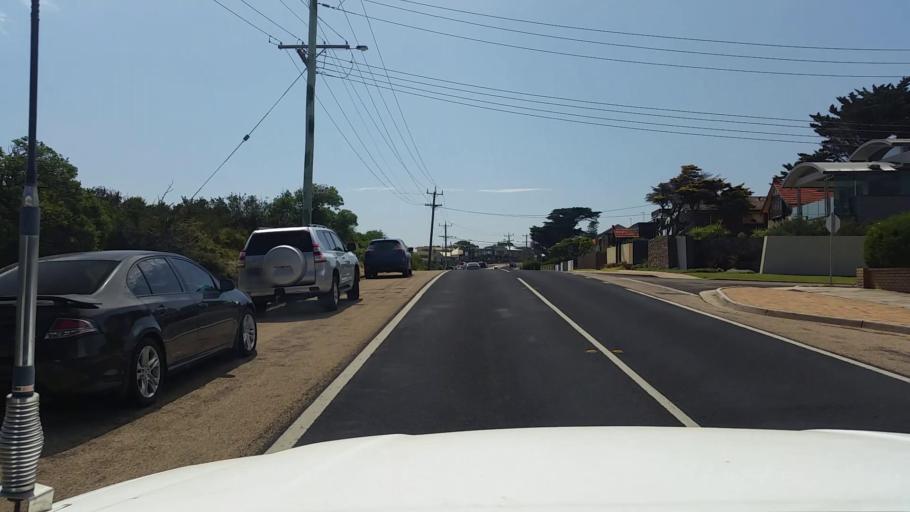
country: AU
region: Victoria
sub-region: Mornington Peninsula
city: Mornington
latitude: -38.2257
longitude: 145.0304
